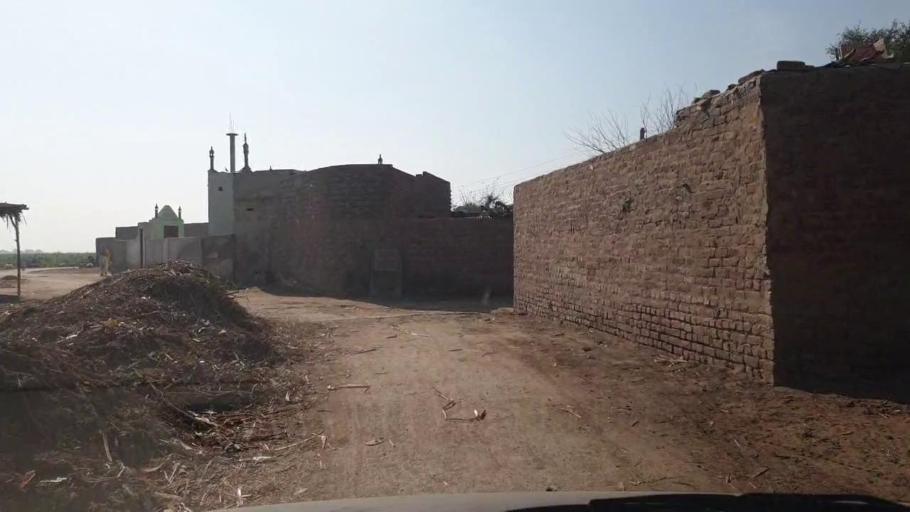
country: PK
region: Sindh
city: Tando Allahyar
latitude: 25.4110
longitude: 68.7420
